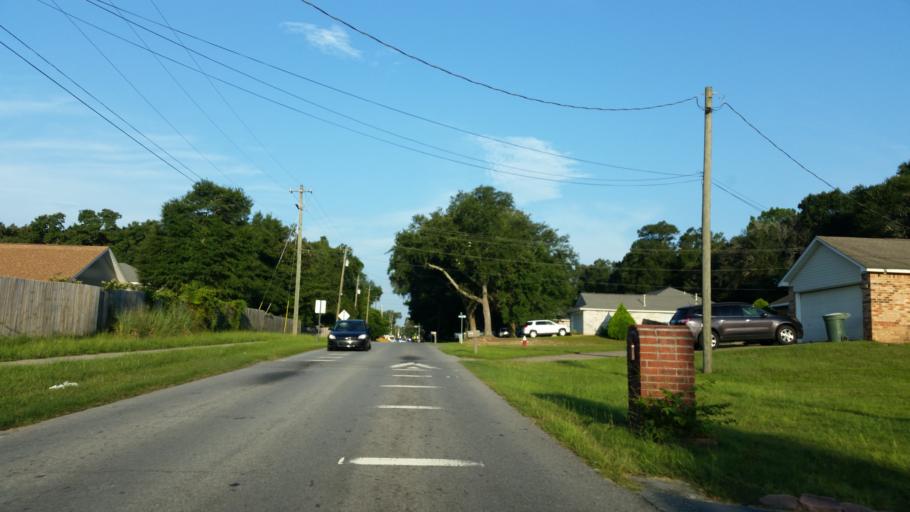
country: US
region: Florida
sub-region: Escambia County
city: Bellview
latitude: 30.4684
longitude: -87.3016
